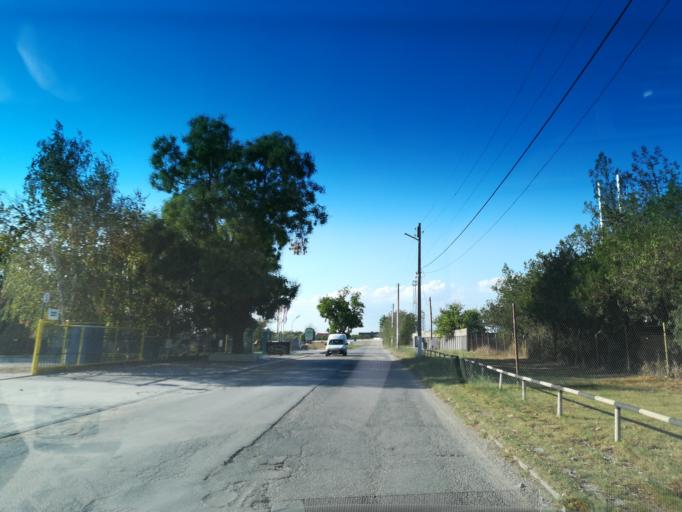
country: BG
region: Stara Zagora
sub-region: Obshtina Chirpan
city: Chirpan
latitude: 42.0905
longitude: 25.2377
